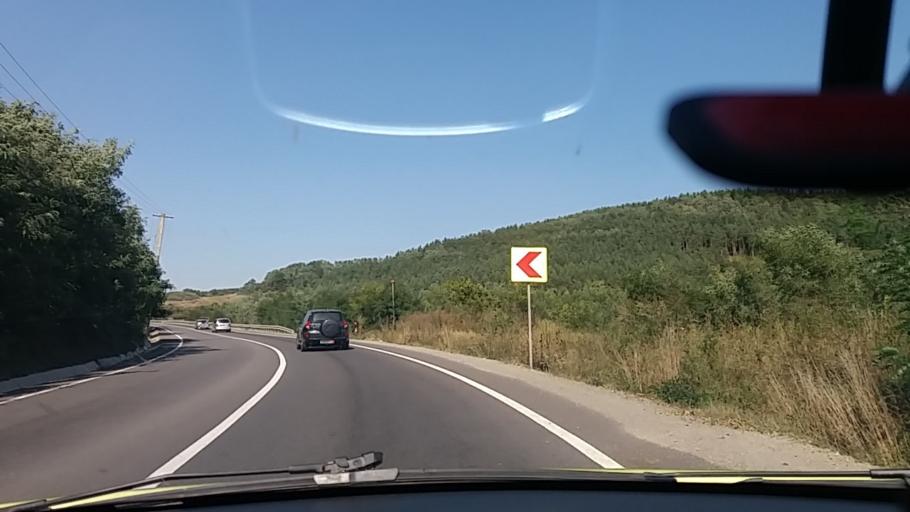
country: RO
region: Sibiu
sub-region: Comuna Slimnic
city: Slimnic
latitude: 45.9266
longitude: 24.1711
